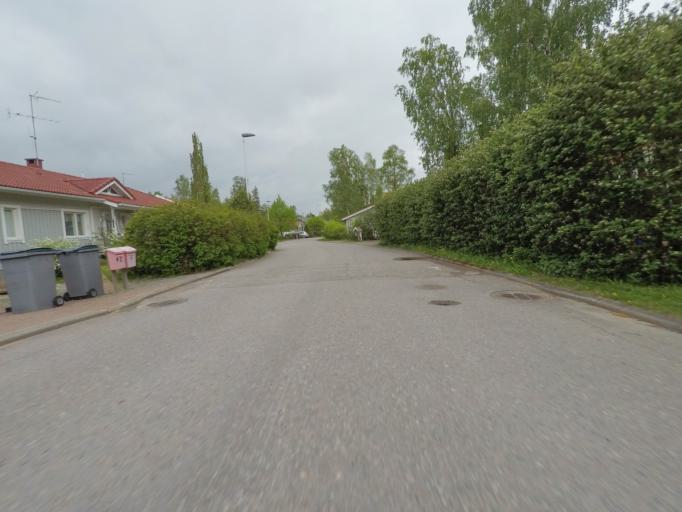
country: FI
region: Uusimaa
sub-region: Helsinki
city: Kirkkonummi
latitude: 60.1269
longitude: 24.4064
